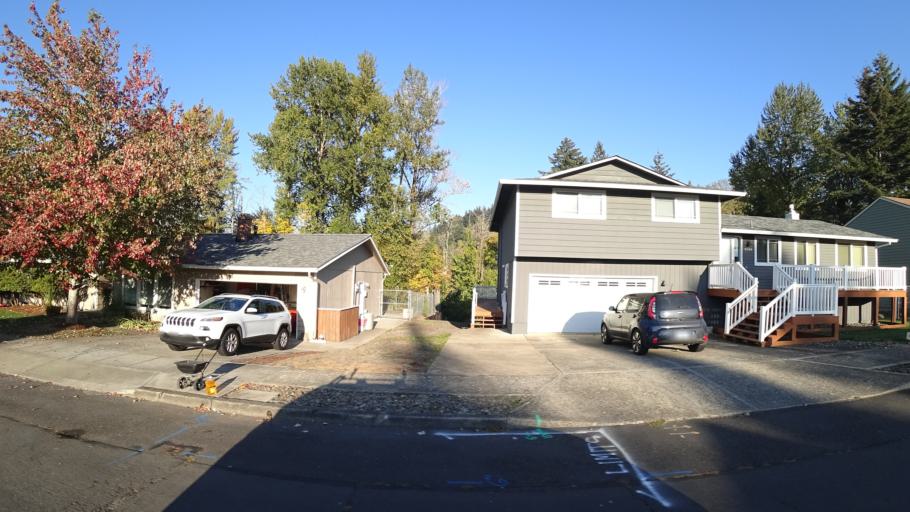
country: US
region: Oregon
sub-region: Multnomah County
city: Gresham
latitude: 45.4866
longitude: -122.4490
